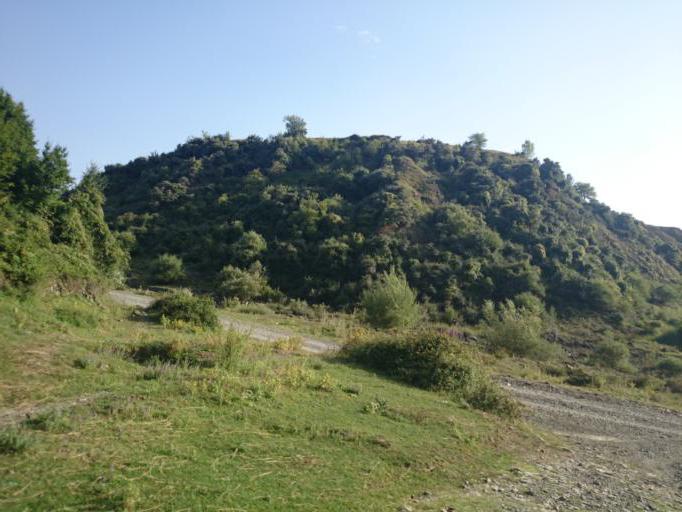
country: AL
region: Elbasan
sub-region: Rrethi i Gramshit
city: Lenias
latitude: 40.7775
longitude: 20.3846
